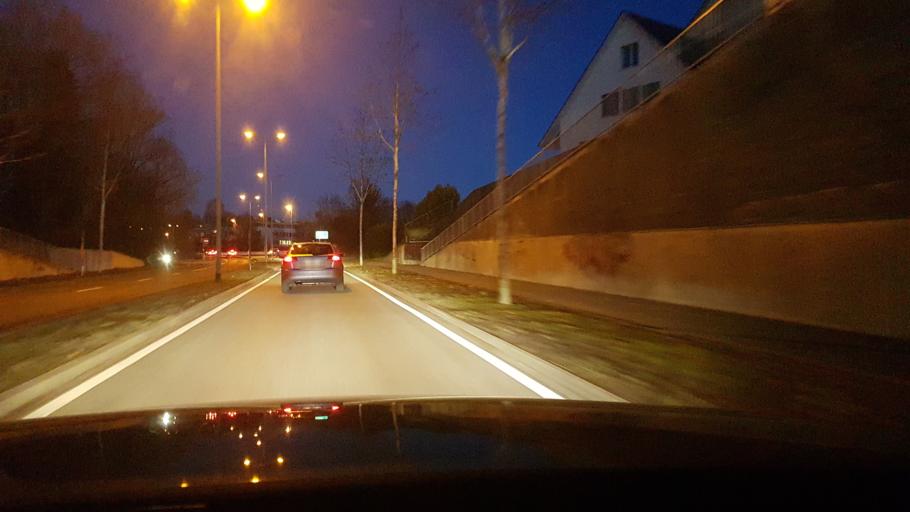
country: CH
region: Zurich
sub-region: Bezirk Buelach
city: Glattbrugg / Wydacker/Bettacker/Laettenwiesen
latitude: 47.4273
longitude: 8.5699
